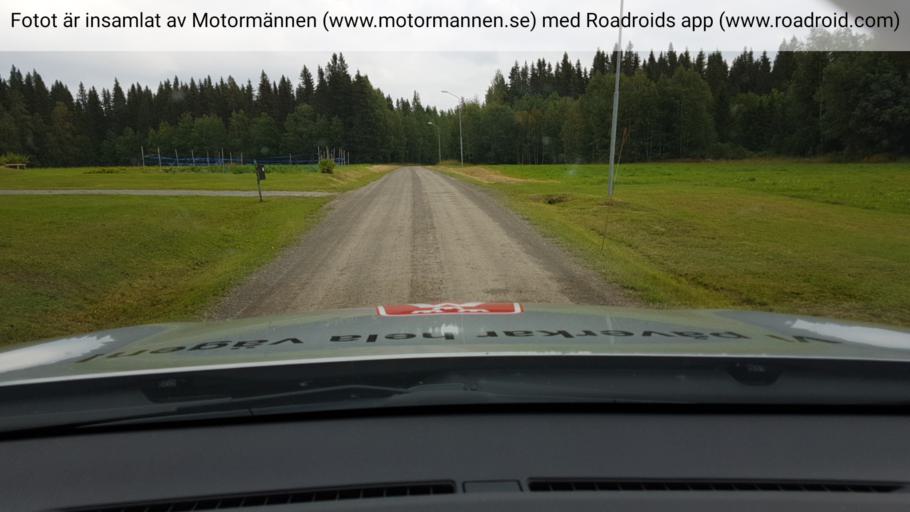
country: SE
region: Jaemtland
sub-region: Stroemsunds Kommun
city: Stroemsund
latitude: 63.7665
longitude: 15.3365
